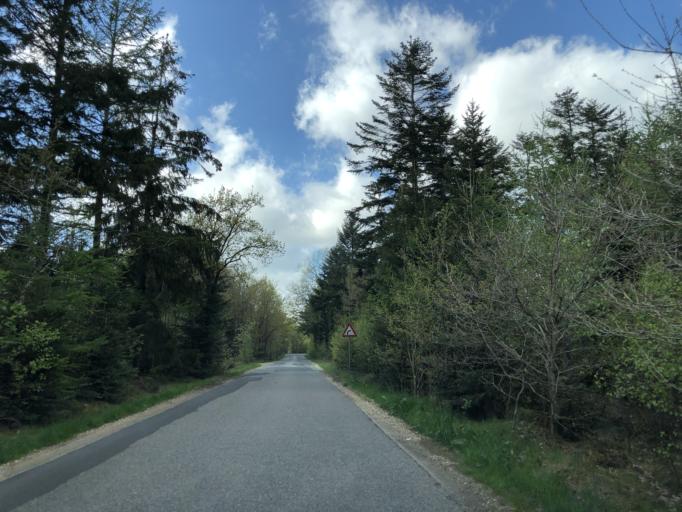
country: DK
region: Central Jutland
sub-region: Herning Kommune
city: Avlum
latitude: 56.3000
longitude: 8.6979
